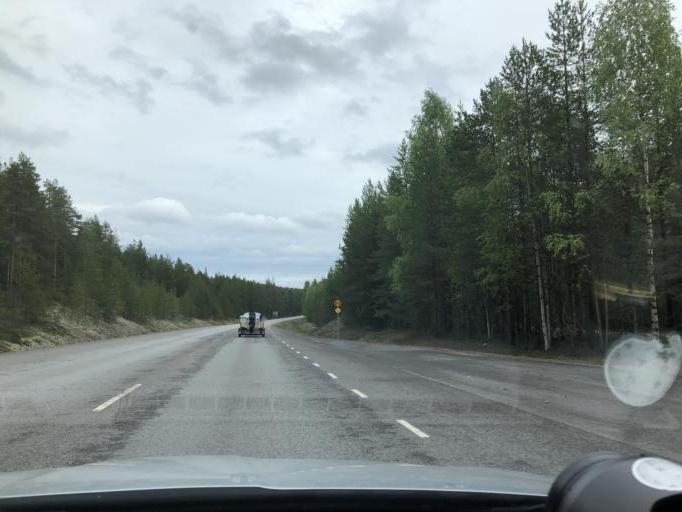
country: SE
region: Norrbotten
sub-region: Pitea Kommun
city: Pitea
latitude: 65.2695
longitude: 21.5304
